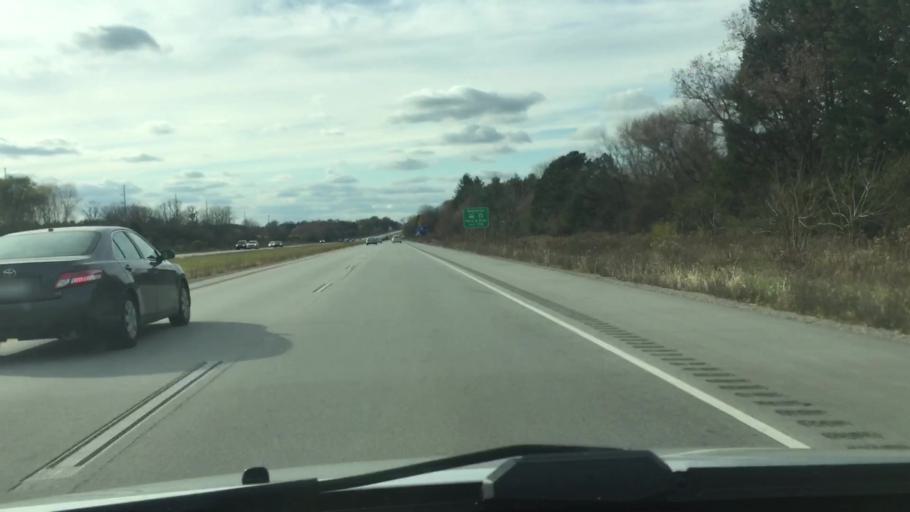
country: US
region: Wisconsin
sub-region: Waukesha County
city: Nashotah
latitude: 43.1032
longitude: -88.3760
